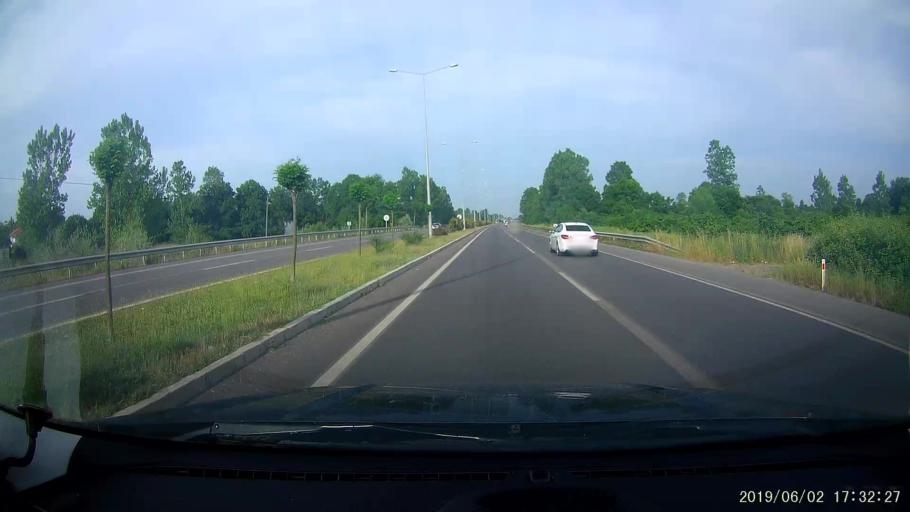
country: TR
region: Samsun
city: Carsamba
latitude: 41.2200
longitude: 36.8266
